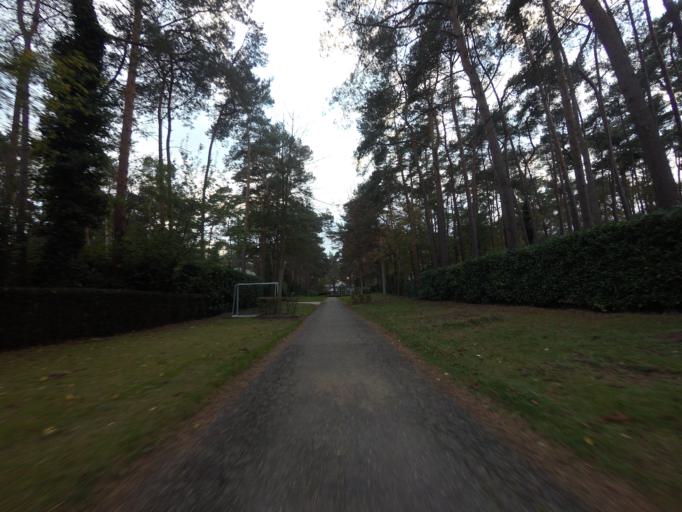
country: BE
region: Flanders
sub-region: Provincie Antwerpen
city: Bonheiden
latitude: 51.0205
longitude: 4.5818
